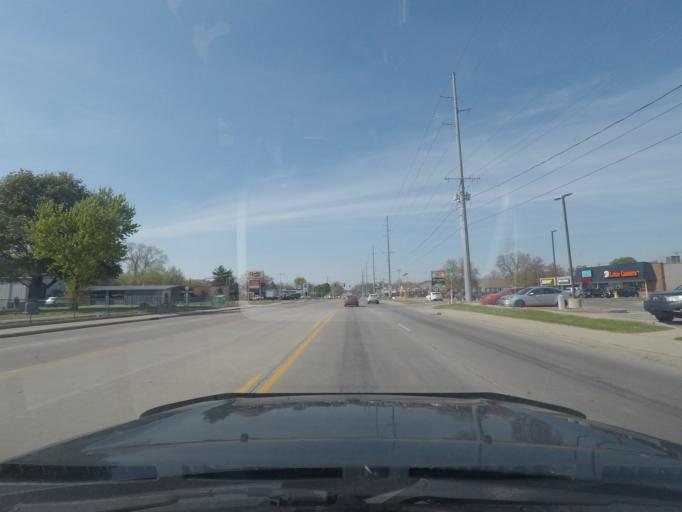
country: US
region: Indiana
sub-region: Elkhart County
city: Elkhart
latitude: 41.6727
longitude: -86.0032
